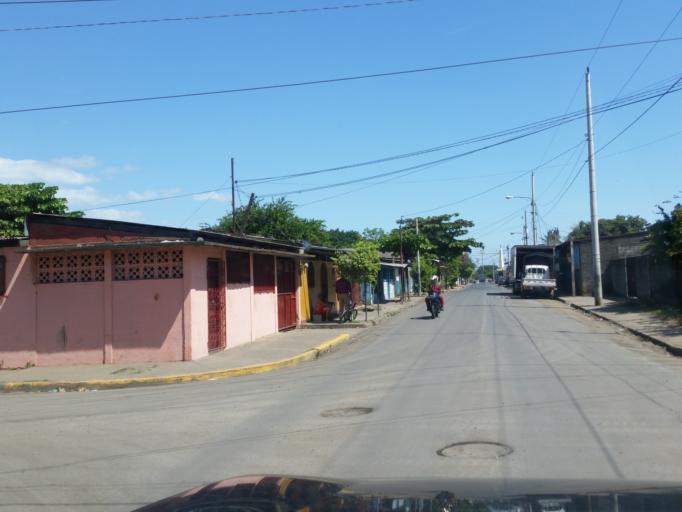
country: NI
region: Managua
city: Managua
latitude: 12.1593
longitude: -86.2803
